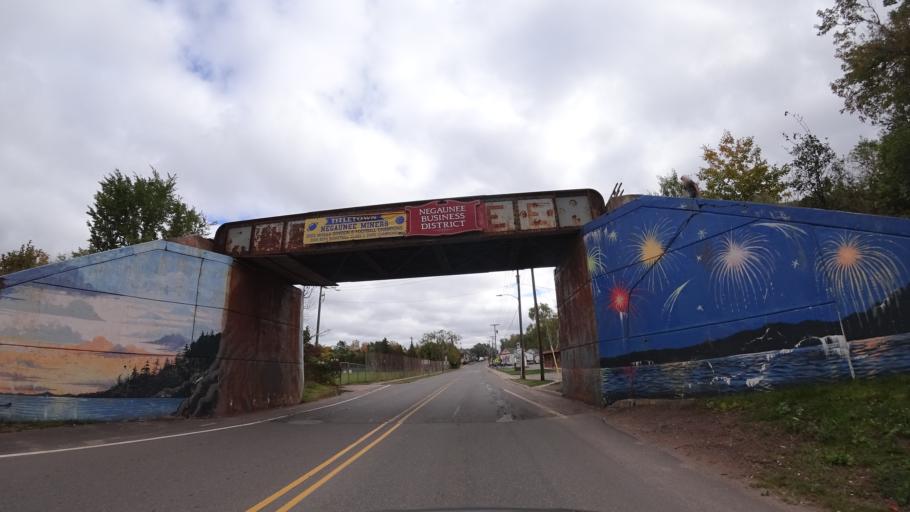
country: US
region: Michigan
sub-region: Marquette County
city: Negaunee
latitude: 46.5062
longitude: -87.6125
